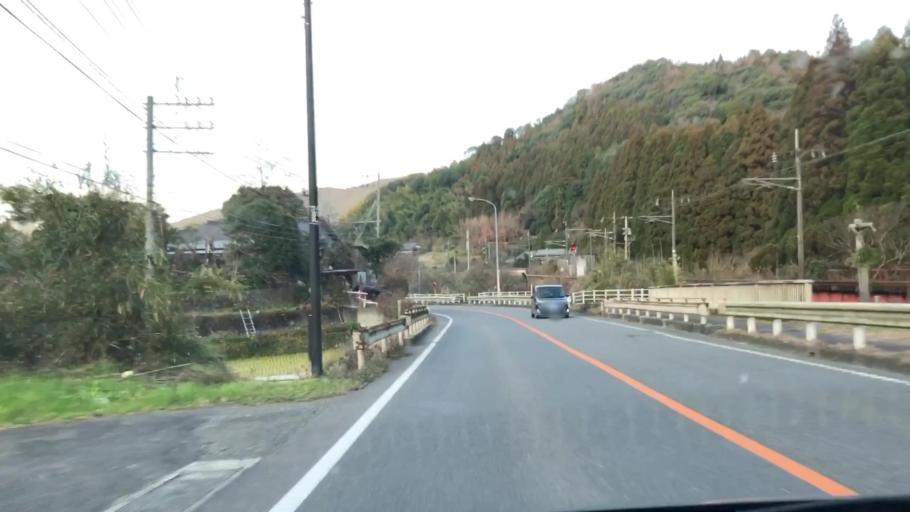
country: JP
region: Kumamoto
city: Minamata
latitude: 32.2192
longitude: 130.4381
